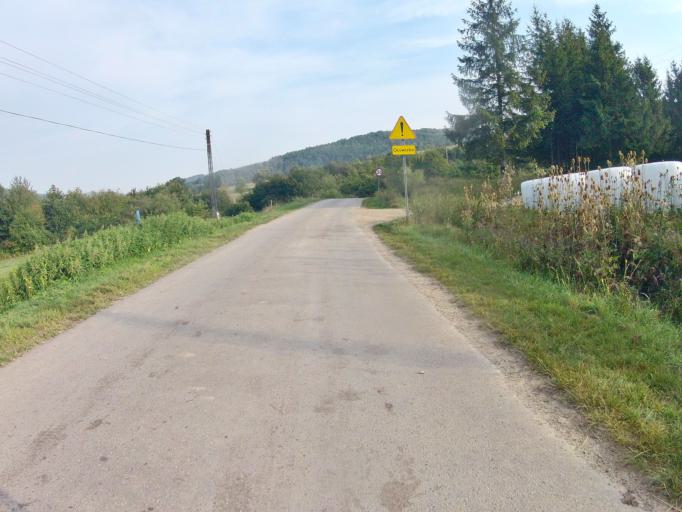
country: PL
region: Subcarpathian Voivodeship
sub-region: Powiat jasielski
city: Krempna
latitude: 49.5438
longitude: 21.5521
